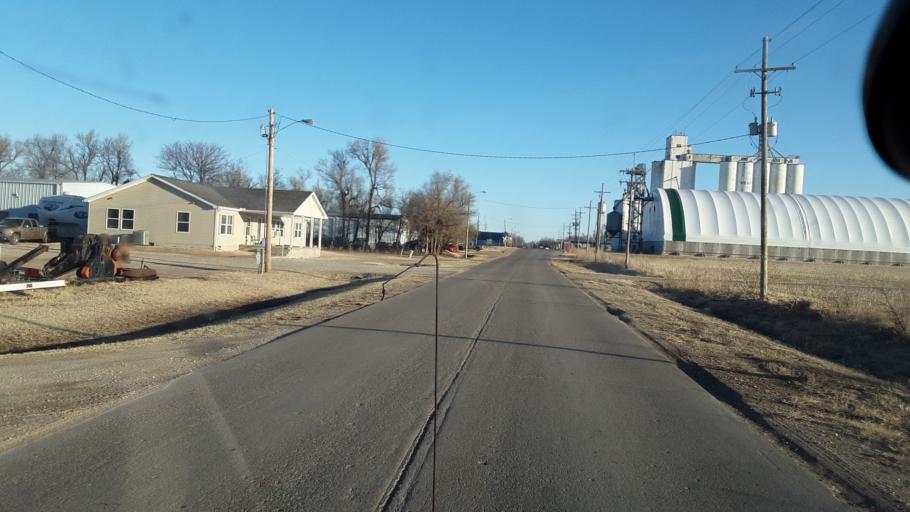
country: US
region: Kansas
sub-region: Rice County
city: Lyons
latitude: 38.3500
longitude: -98.3495
